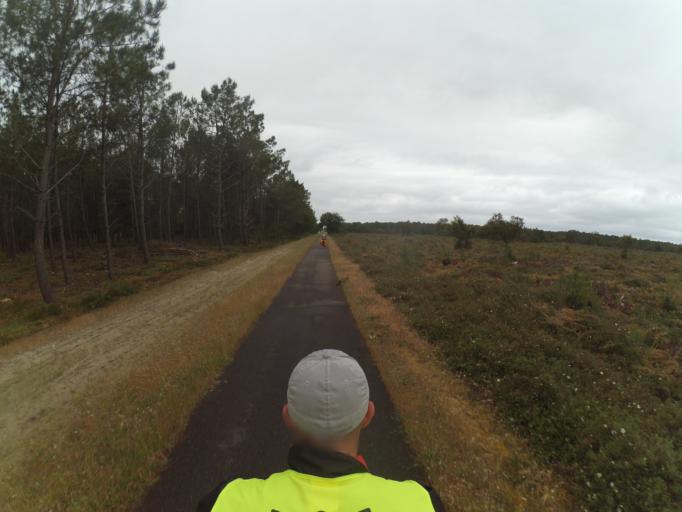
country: FR
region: Aquitaine
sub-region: Departement des Landes
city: Mimizan
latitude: 44.2190
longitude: -1.2776
